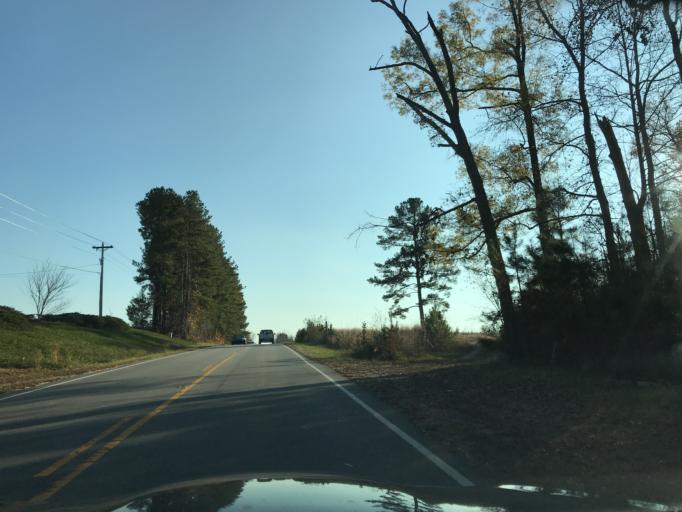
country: US
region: North Carolina
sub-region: Granville County
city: Creedmoor
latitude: 36.1095
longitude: -78.6881
